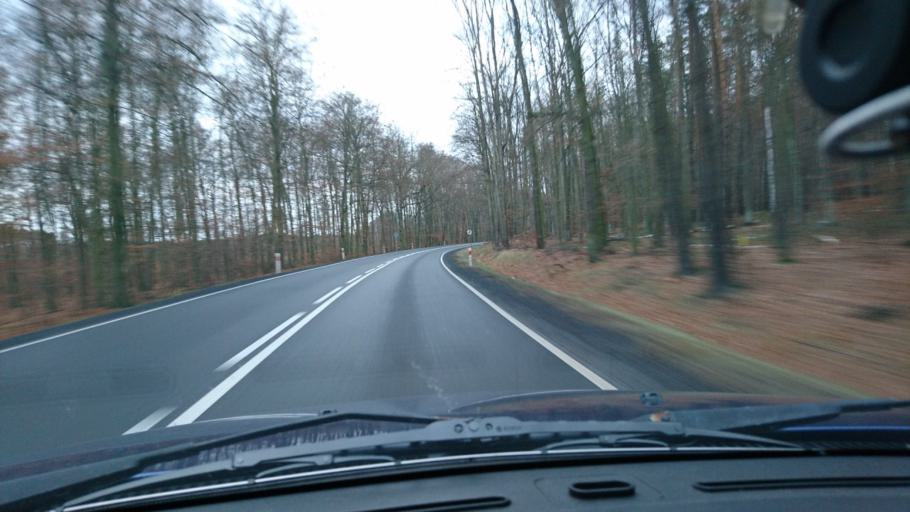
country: PL
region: Opole Voivodeship
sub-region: Powiat kluczborski
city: Kluczbork
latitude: 50.9613
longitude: 18.2908
